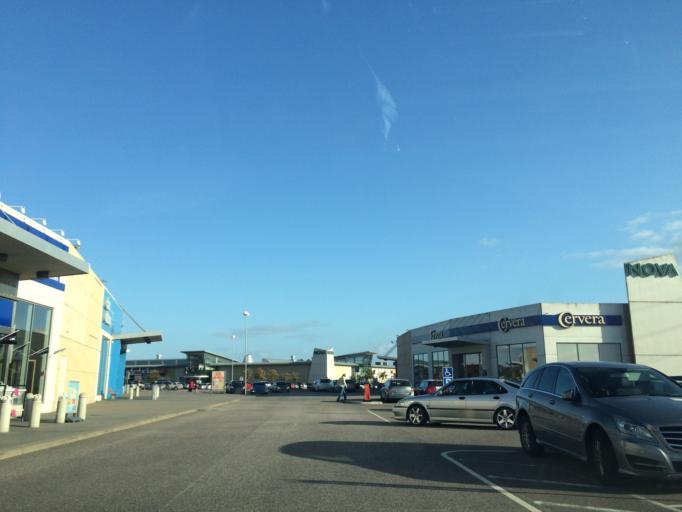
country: SE
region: Skane
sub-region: Lunds Kommun
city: Lund
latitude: 55.7151
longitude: 13.1562
